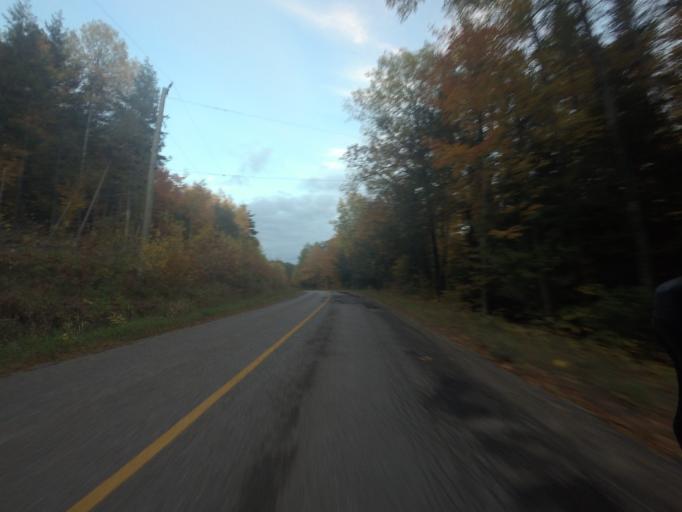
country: CA
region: Ontario
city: Renfrew
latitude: 45.3556
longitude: -76.9571
